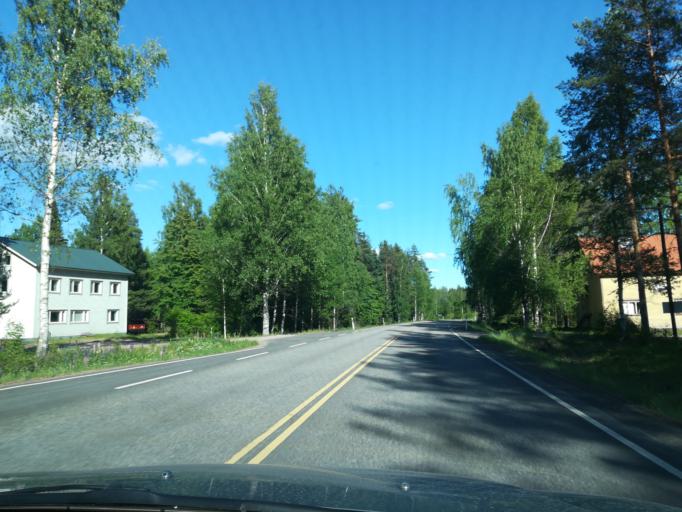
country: FI
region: South Karelia
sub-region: Imatra
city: Ruokolahti
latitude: 61.3994
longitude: 28.6252
